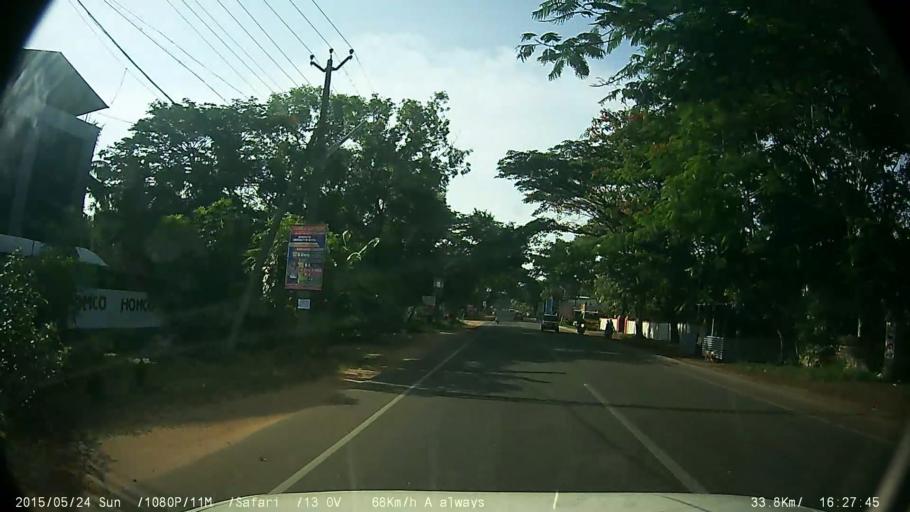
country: IN
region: Kerala
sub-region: Alappuzha
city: Alleppey
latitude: 9.5317
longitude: 76.3274
